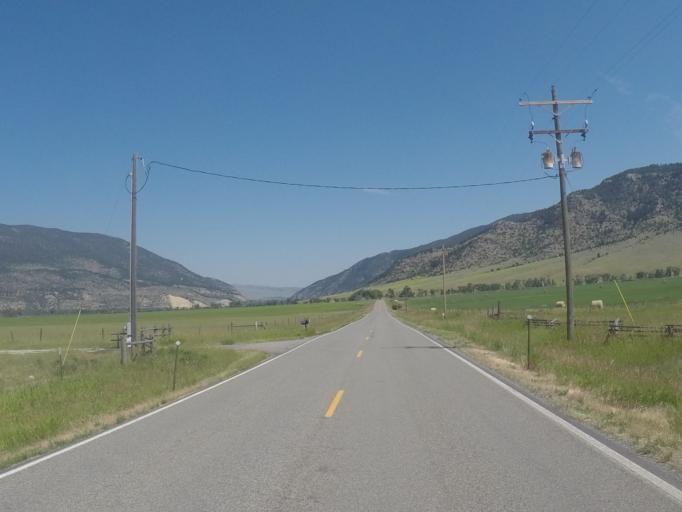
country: US
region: Montana
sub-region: Park County
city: Livingston
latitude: 45.5584
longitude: -110.5589
